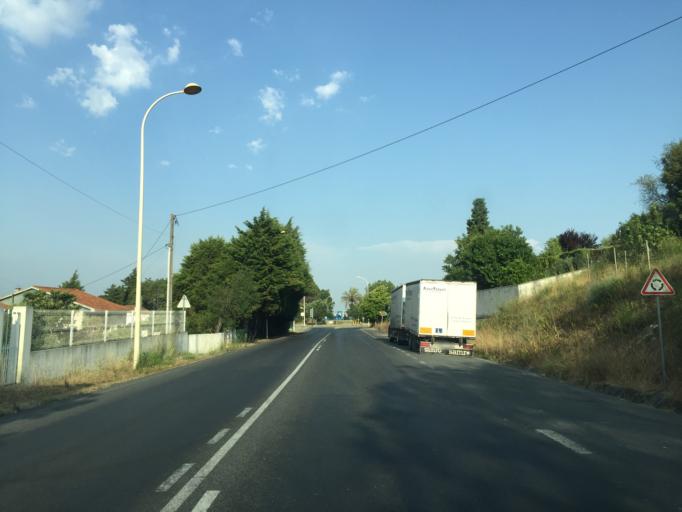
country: PT
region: Santarem
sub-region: Torres Novas
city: Torres Novas
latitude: 39.4757
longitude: -8.5617
